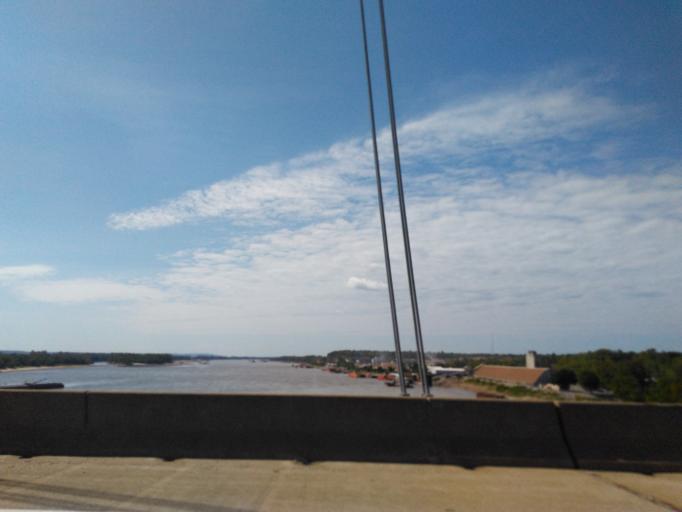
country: US
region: Missouri
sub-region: Saint Louis County
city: Oakville
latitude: 38.4869
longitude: -90.2768
